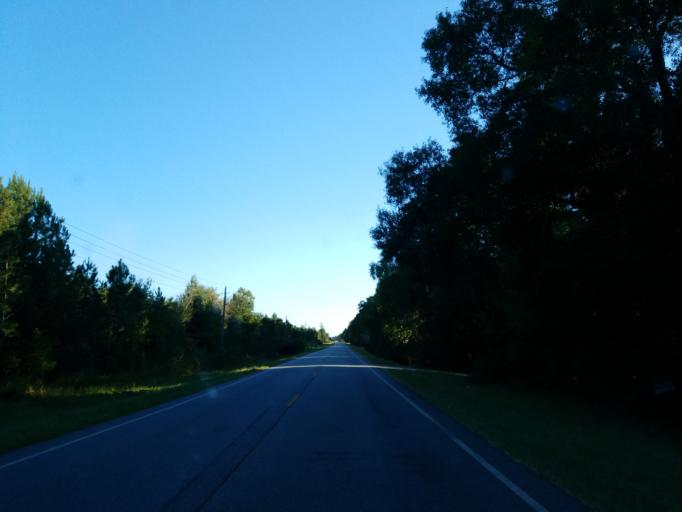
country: US
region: Georgia
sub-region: Worth County
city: Sylvester
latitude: 31.6379
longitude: -83.8658
